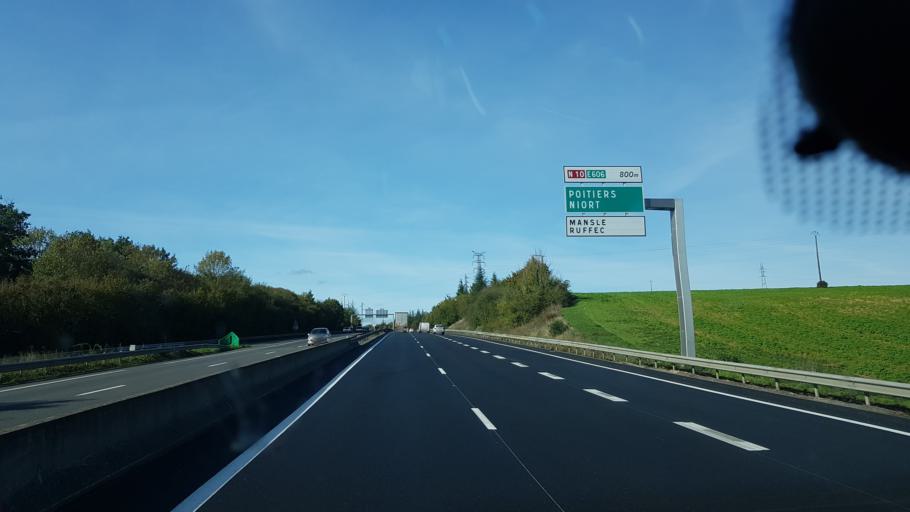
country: FR
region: Poitou-Charentes
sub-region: Departement de la Charente
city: Gond-Pontouvre
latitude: 45.6911
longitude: 0.1917
